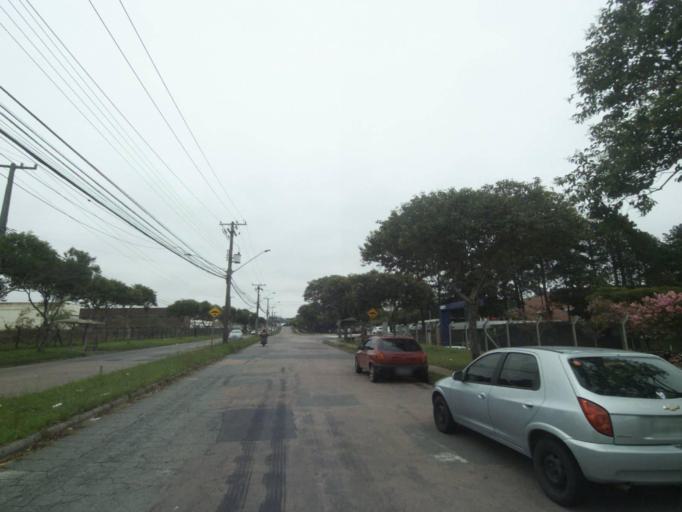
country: BR
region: Parana
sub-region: Sao Jose Dos Pinhais
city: Sao Jose dos Pinhais
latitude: -25.5312
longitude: -49.3148
